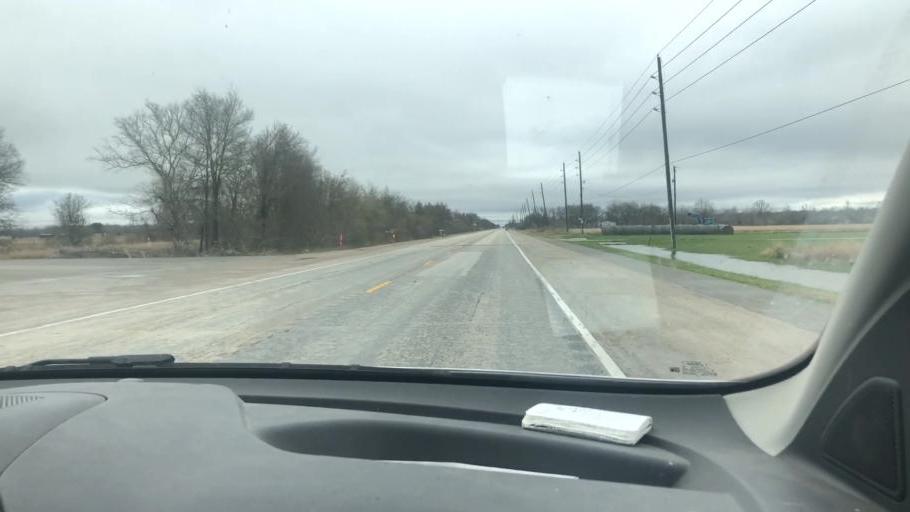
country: US
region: Texas
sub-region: Wharton County
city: Wharton
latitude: 29.2851
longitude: -96.0690
